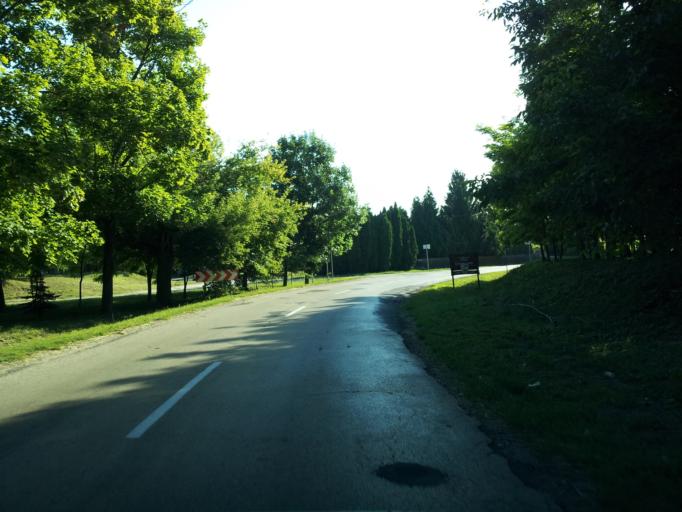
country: HU
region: Fejer
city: Lepseny
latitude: 47.0499
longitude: 18.2416
